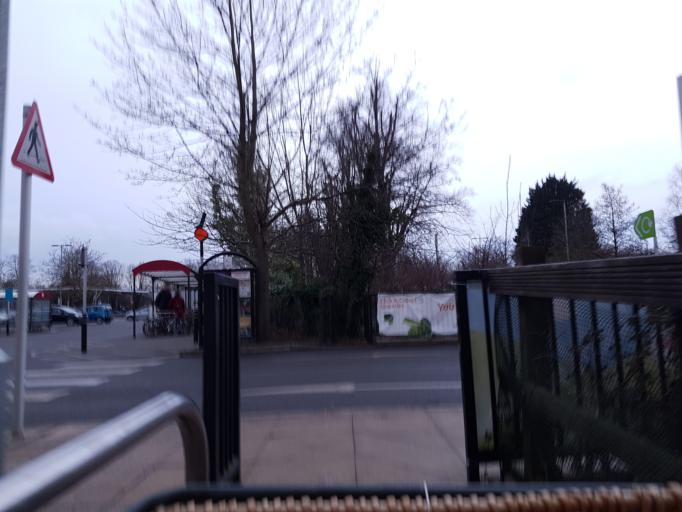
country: GB
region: England
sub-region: Cambridgeshire
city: Cambridge
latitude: 52.1993
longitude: 0.1582
